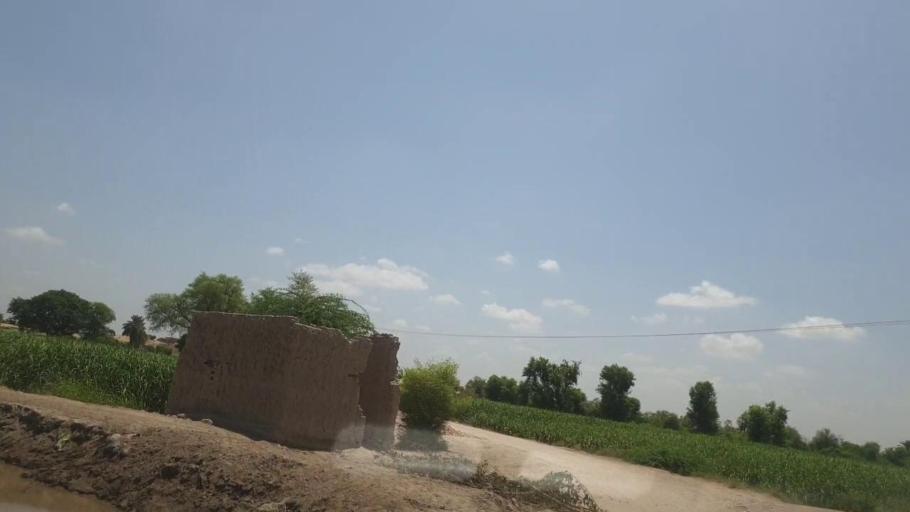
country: PK
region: Sindh
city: Pano Aqil
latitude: 27.6648
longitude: 69.1972
